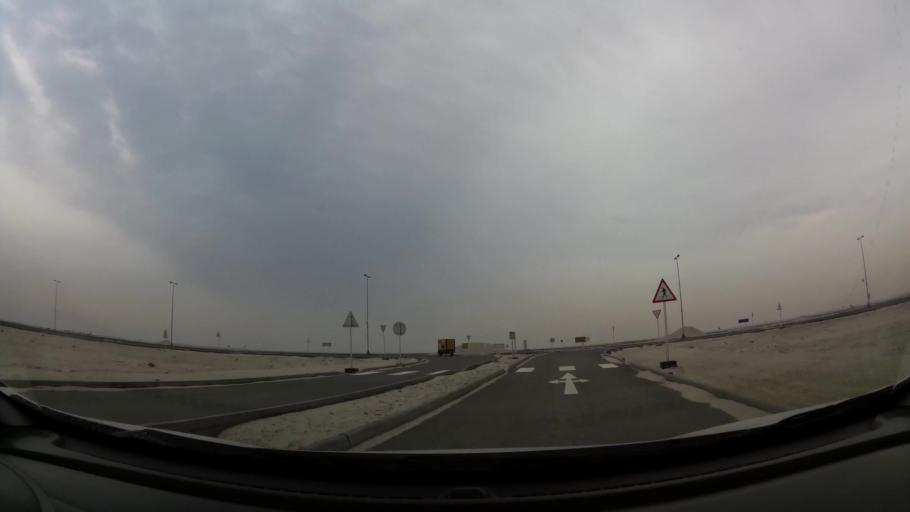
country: BH
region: Central Governorate
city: Dar Kulayb
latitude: 25.8649
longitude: 50.6056
